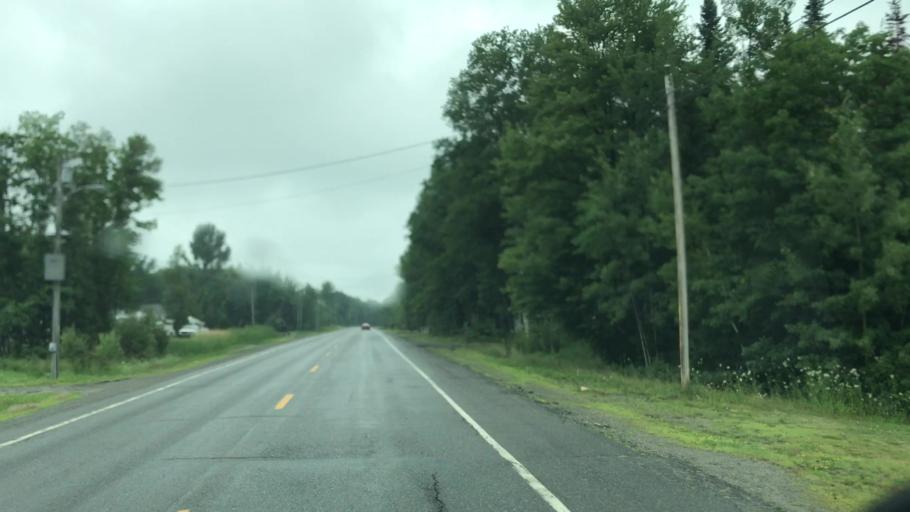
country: US
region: Maine
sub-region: Penobscot County
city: Howland
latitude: 45.2645
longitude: -68.6384
